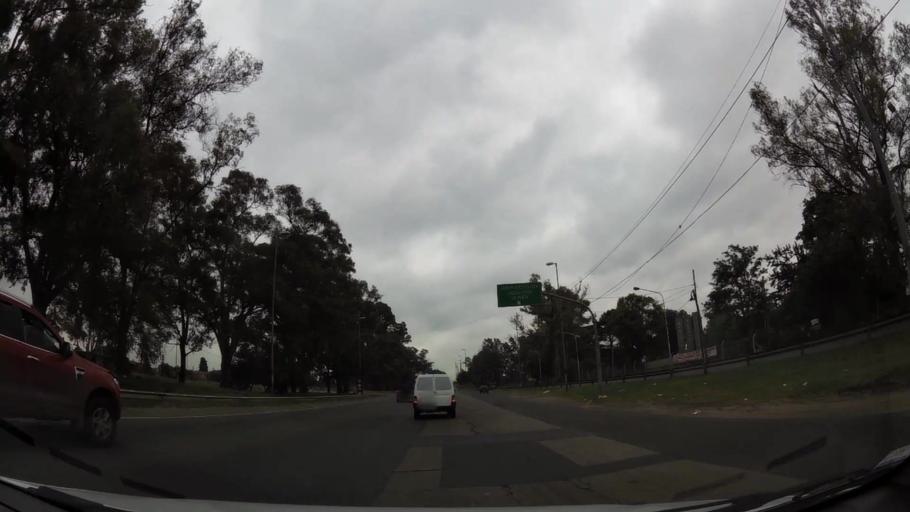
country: AR
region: Buenos Aires F.D.
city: Villa Lugano
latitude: -34.7199
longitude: -58.5154
